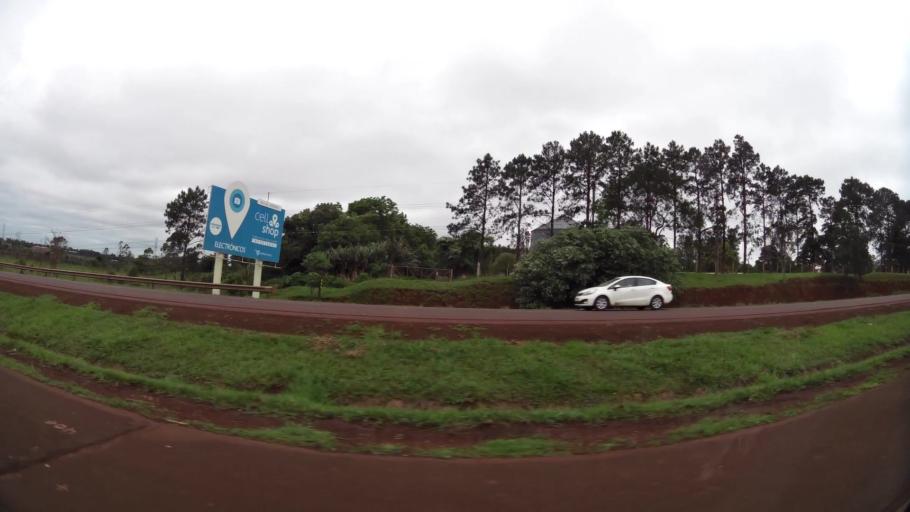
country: PY
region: Alto Parana
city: Colonia Yguazu
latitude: -25.4879
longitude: -54.8317
